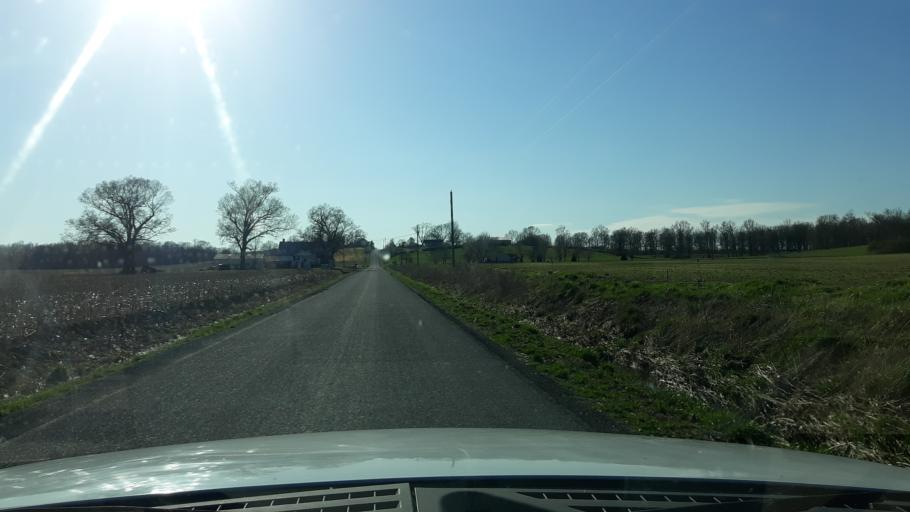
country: US
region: Illinois
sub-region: Saline County
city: Harrisburg
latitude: 37.7756
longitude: -88.5882
